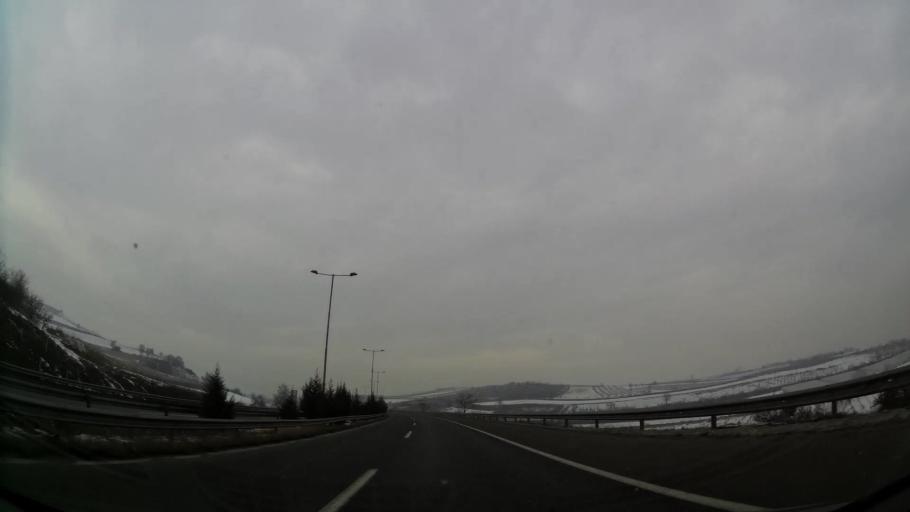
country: MK
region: Saraj
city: Saraj
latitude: 42.0155
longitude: 21.3311
